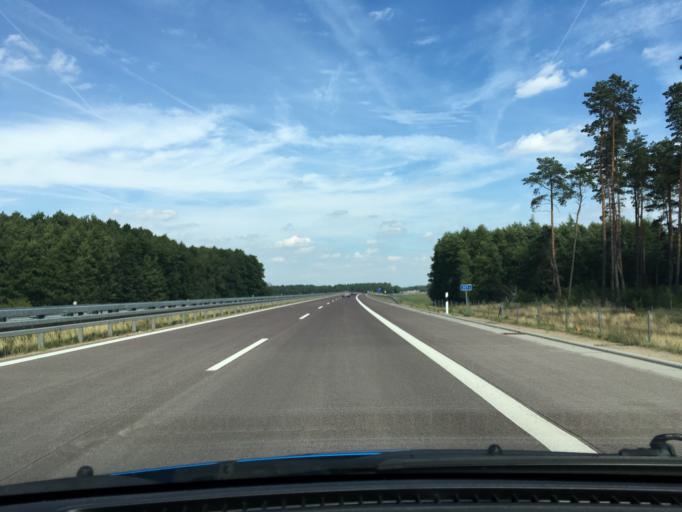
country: DE
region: Mecklenburg-Vorpommern
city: Gross Laasch
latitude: 53.3721
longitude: 11.5185
